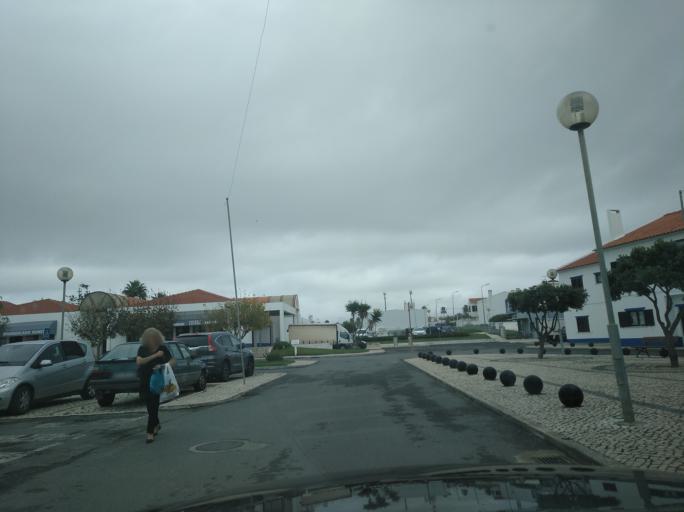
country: PT
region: Setubal
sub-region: Sines
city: Porto Covo
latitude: 37.8515
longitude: -8.7909
